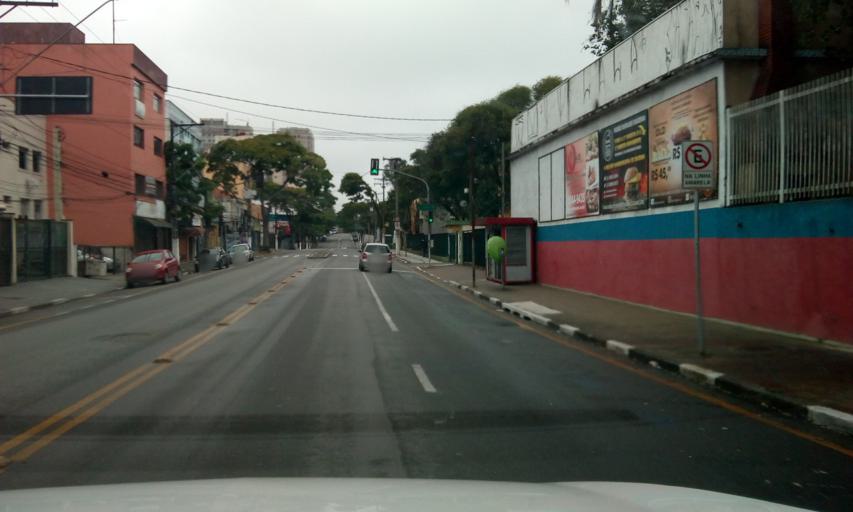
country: BR
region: Sao Paulo
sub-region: Diadema
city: Diadema
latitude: -23.6911
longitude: -46.6180
